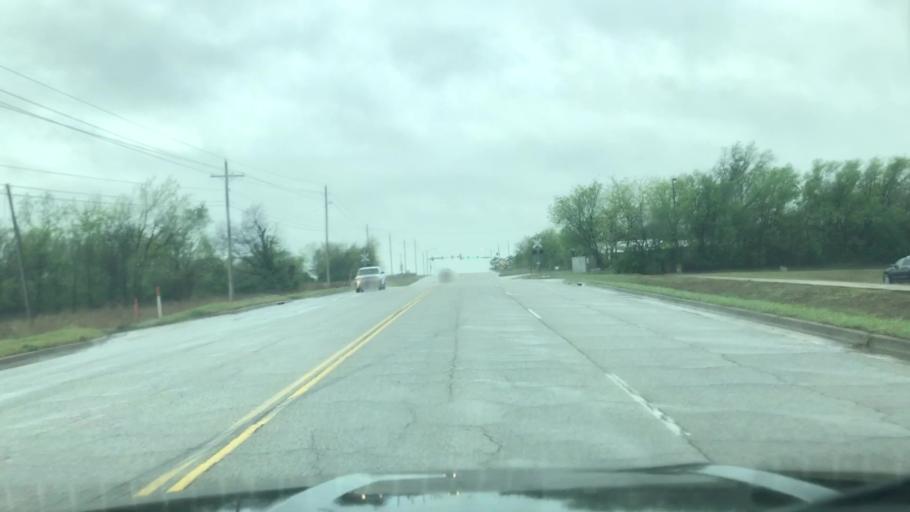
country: US
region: Oklahoma
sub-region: Tulsa County
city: Owasso
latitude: 36.2641
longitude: -95.8874
